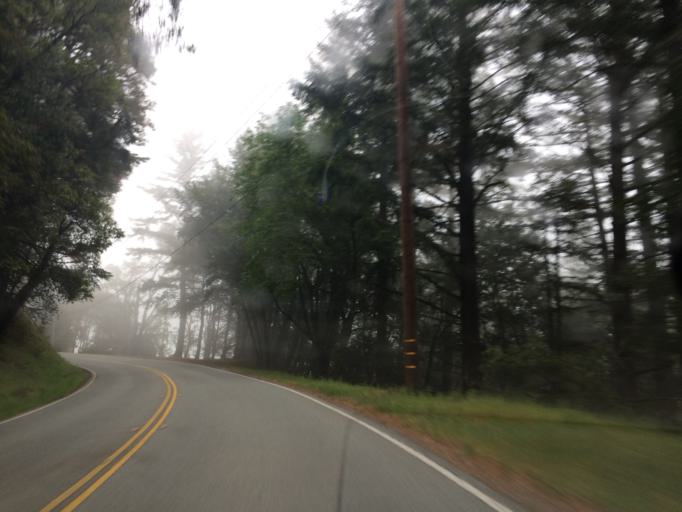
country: US
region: California
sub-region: Santa Clara County
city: Loyola
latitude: 37.2764
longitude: -122.1505
